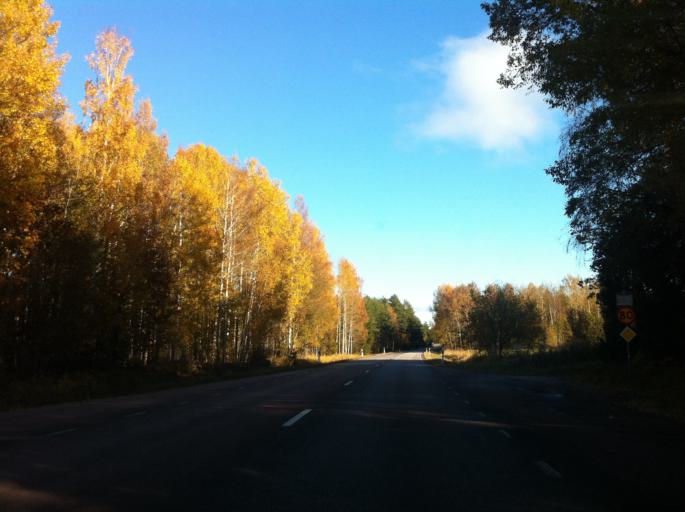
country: SE
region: Uppsala
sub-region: Osthammars Kommun
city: OEsthammar
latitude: 60.3261
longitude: 18.3425
